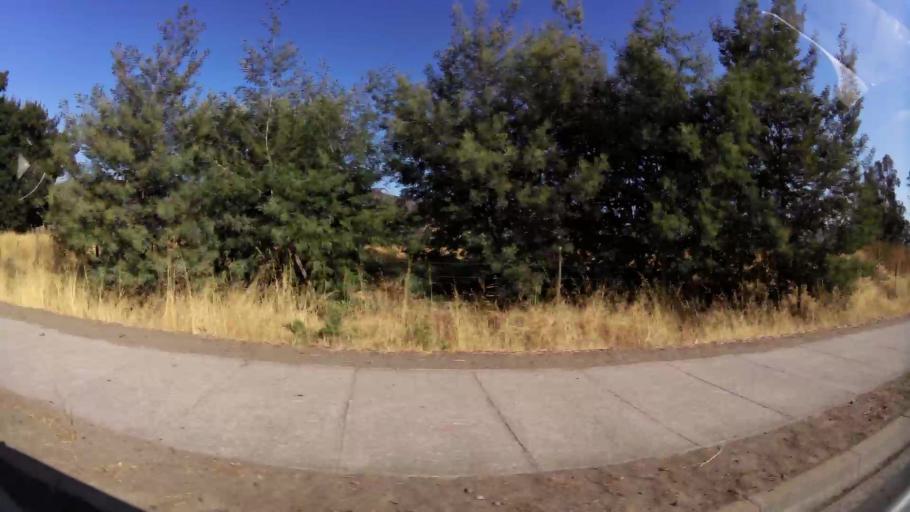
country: CL
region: Maule
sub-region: Provincia de Talca
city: Talca
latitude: -35.4115
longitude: -71.6700
